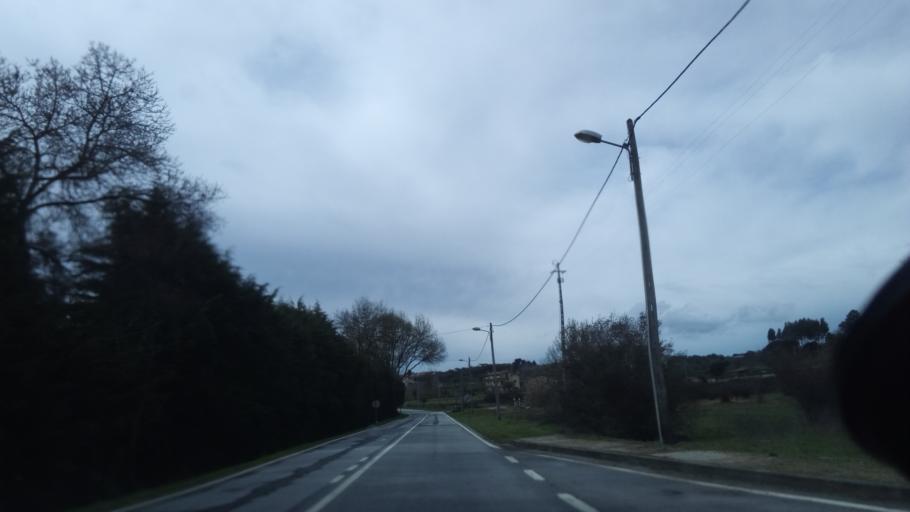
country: PT
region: Guarda
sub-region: Seia
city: Seia
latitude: 40.4527
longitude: -7.7043
